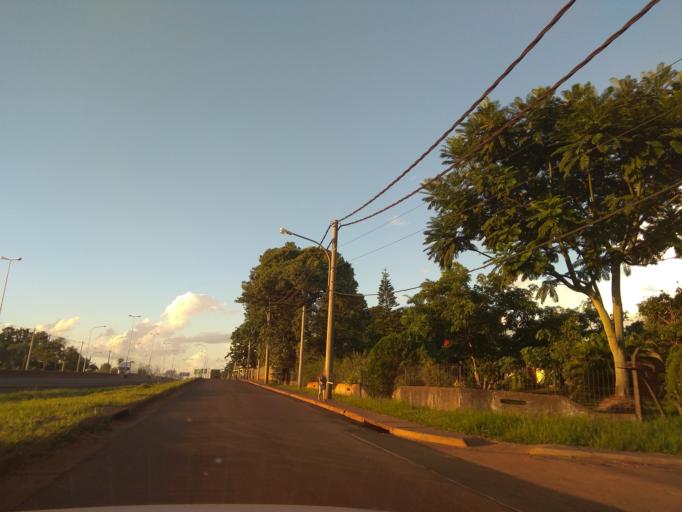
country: AR
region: Misiones
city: Garupa
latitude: -27.4626
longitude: -55.8627
